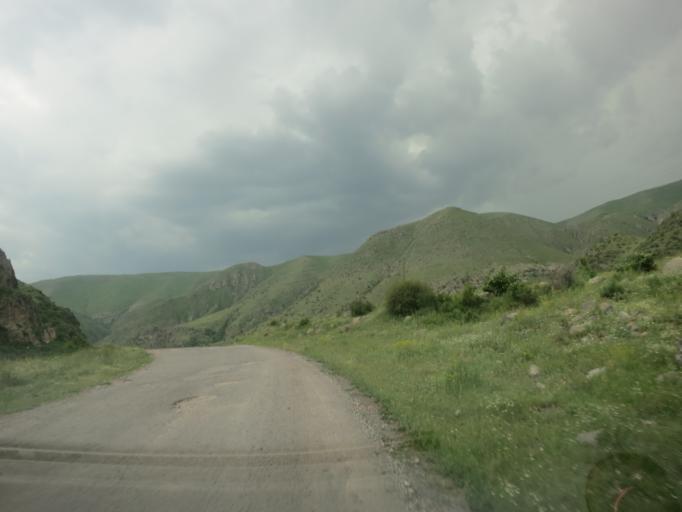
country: TR
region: Ardahan
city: Kurtkale
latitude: 41.3733
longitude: 43.2660
